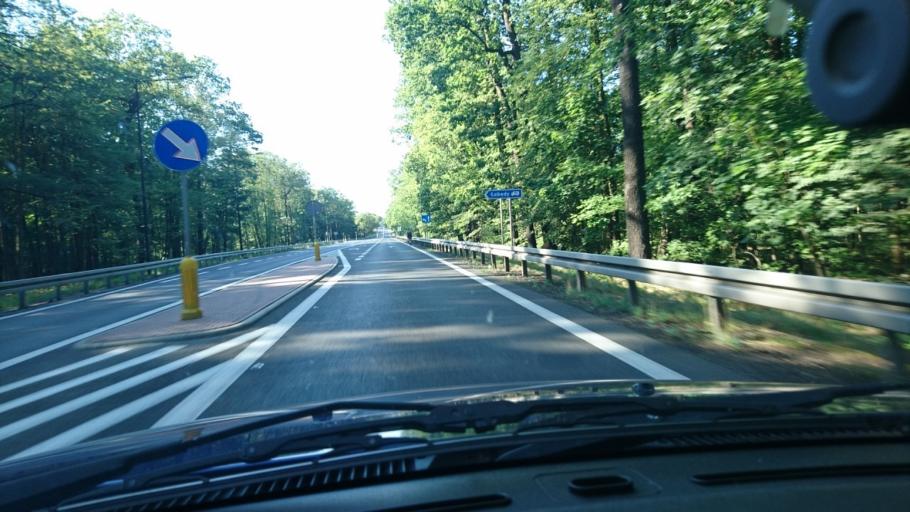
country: PL
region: Silesian Voivodeship
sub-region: Powiat gliwicki
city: Pyskowice
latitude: 50.3516
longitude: 18.6463
